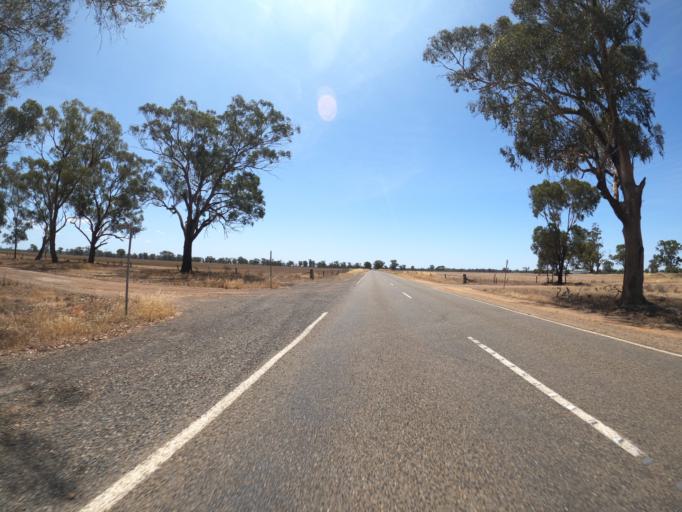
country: AU
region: Victoria
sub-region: Moira
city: Yarrawonga
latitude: -36.1789
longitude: 145.9672
